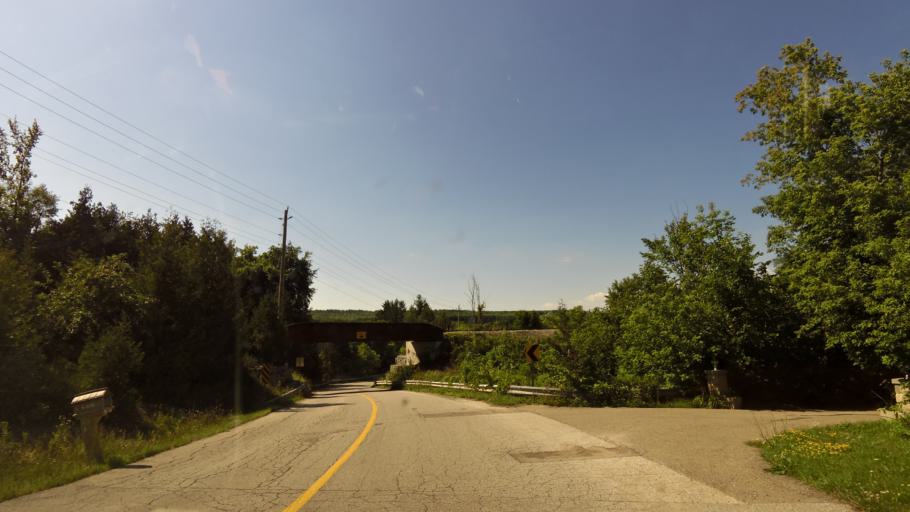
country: CA
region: Ontario
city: Brampton
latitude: 43.7709
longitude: -79.9226
